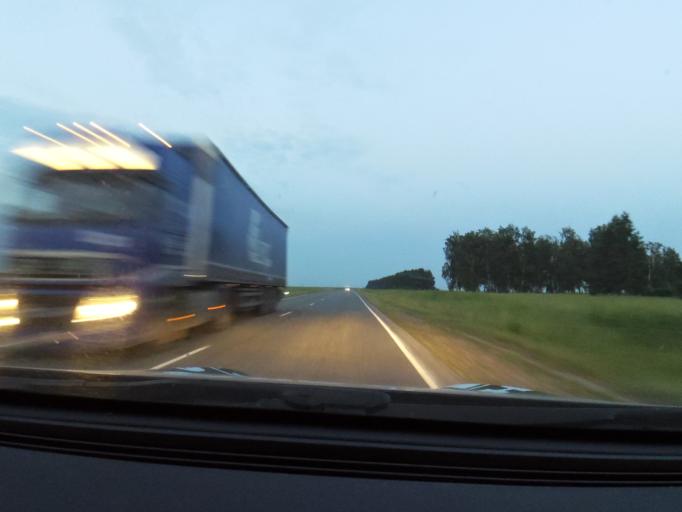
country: RU
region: Bashkortostan
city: Duvan
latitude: 56.1230
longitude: 58.0276
